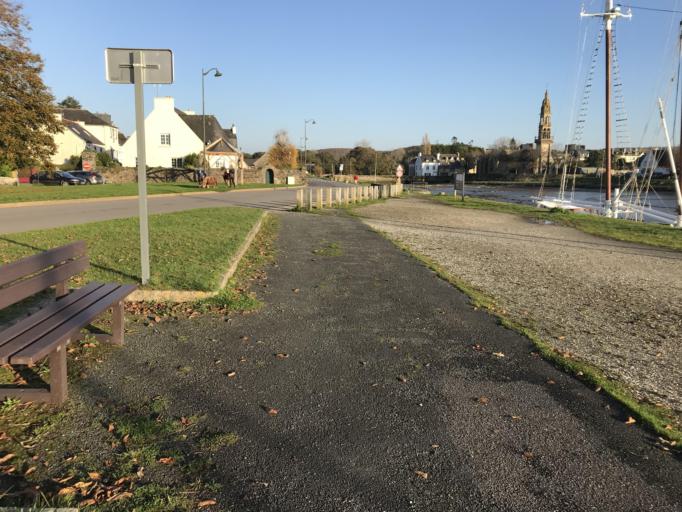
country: FR
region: Brittany
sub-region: Departement du Finistere
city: Le Faou
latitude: 48.2966
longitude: -4.1845
